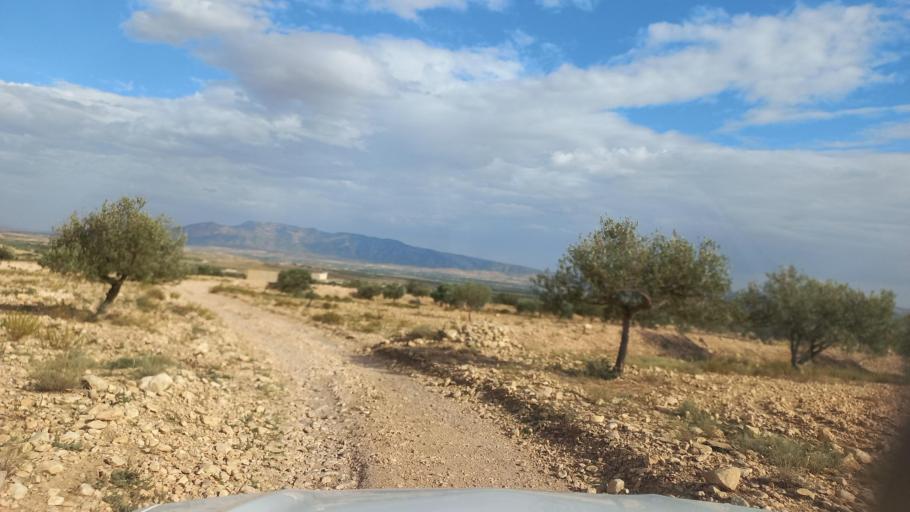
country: TN
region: Al Qasrayn
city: Sbiba
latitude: 35.4507
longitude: 9.0783
